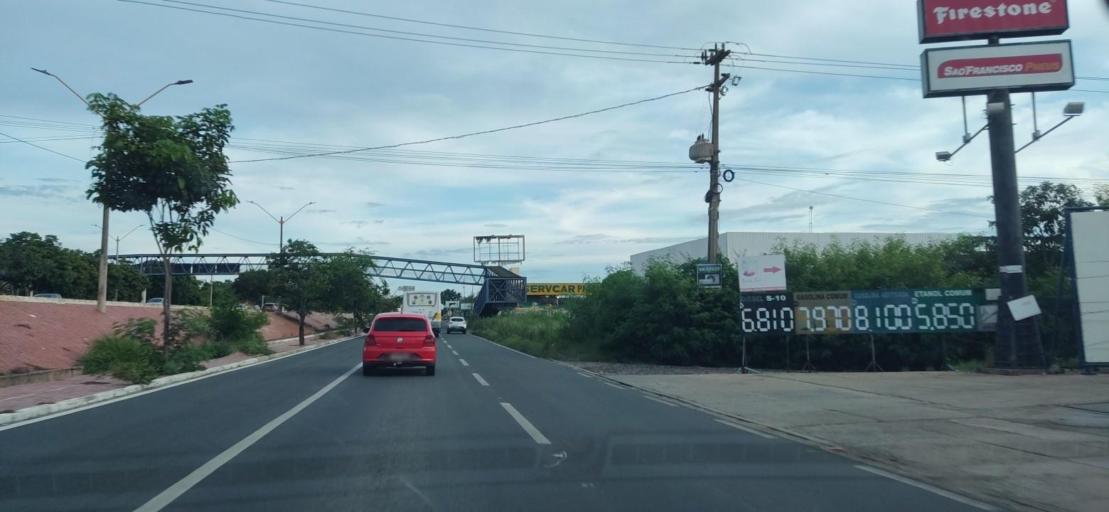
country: BR
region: Piaui
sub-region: Teresina
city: Teresina
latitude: -5.1287
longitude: -42.7931
